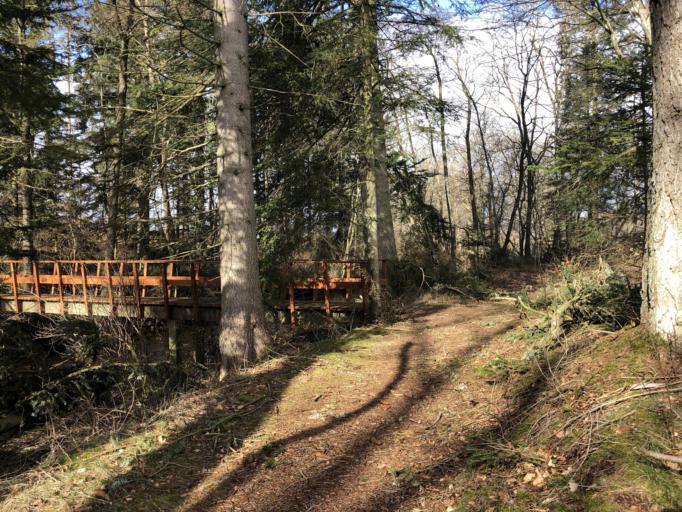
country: DK
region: Central Jutland
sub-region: Herning Kommune
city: Kibaek
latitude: 55.9515
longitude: 8.8755
